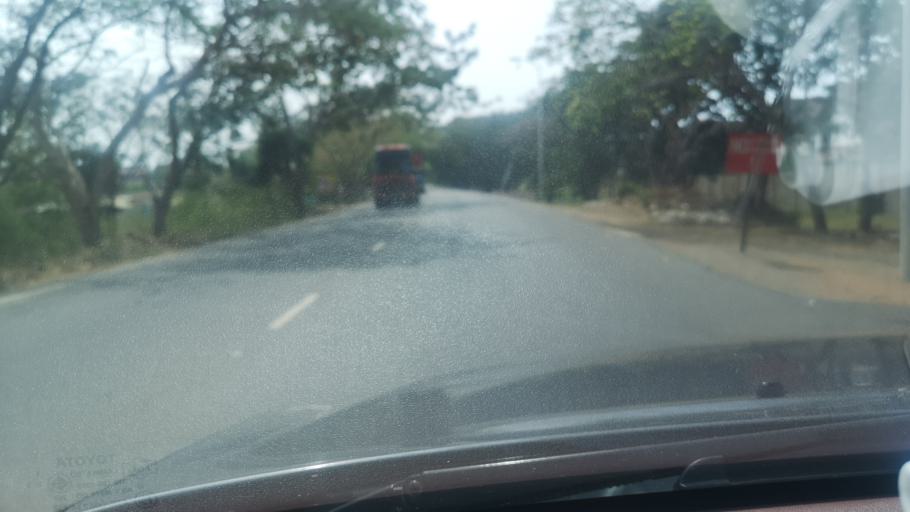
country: GH
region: Greater Accra
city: Nungua
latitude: 5.6148
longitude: -0.0588
